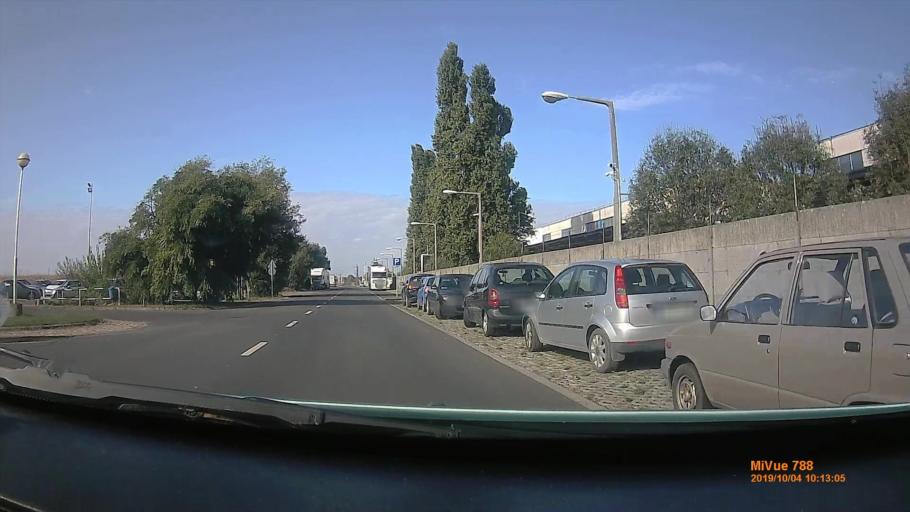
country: HU
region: Szabolcs-Szatmar-Bereg
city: Nyiregyhaza
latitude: 47.9418
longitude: 21.6870
